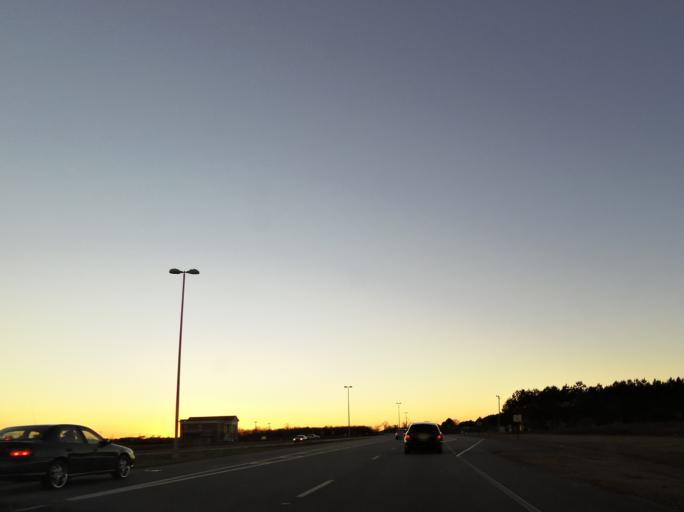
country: US
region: Georgia
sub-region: Houston County
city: Centerville
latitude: 32.5816
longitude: -83.6986
